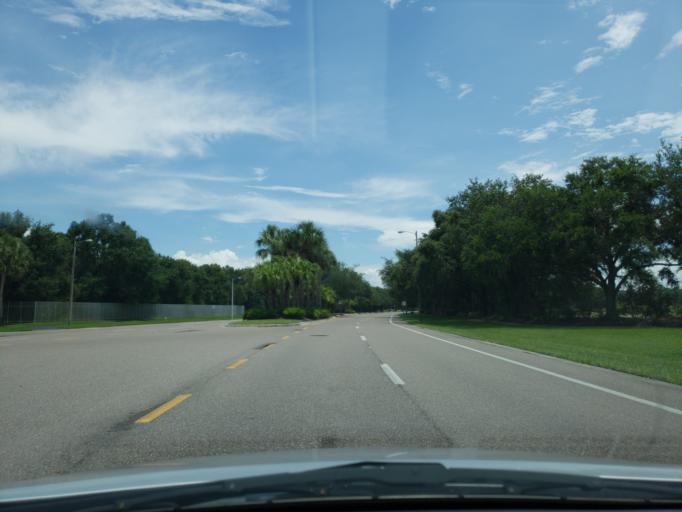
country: US
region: Florida
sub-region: Hillsborough County
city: Pebble Creek
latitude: 28.1211
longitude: -82.3827
